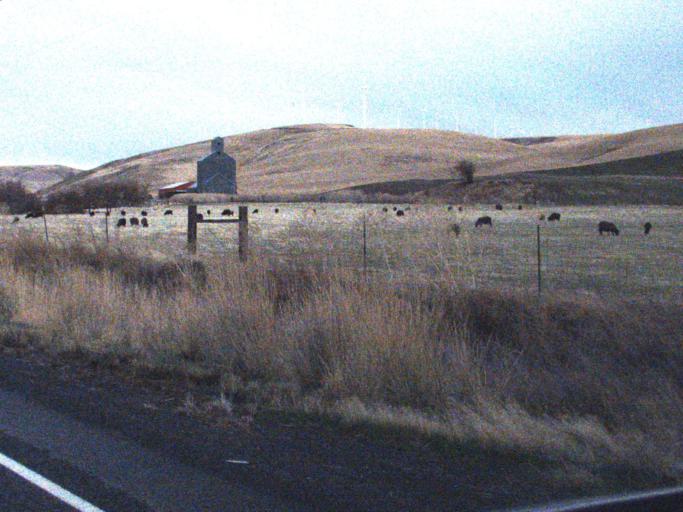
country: US
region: Washington
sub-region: Garfield County
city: Pomeroy
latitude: 46.5254
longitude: -117.8276
